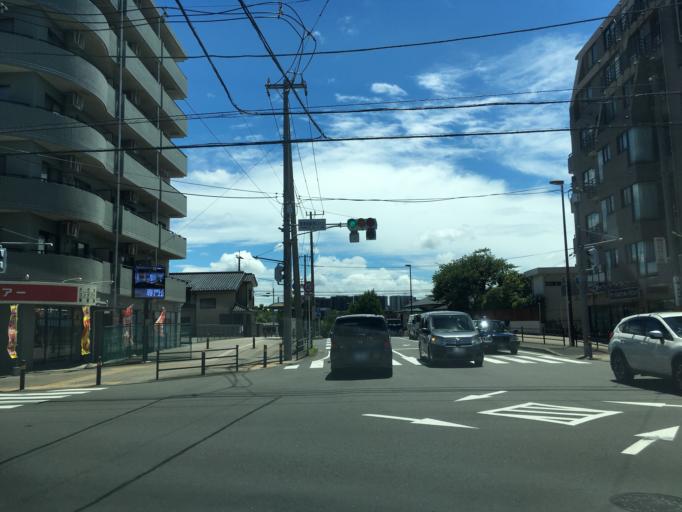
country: JP
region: Tokyo
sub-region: Machida-shi
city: Machida
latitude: 35.5302
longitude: 139.4964
